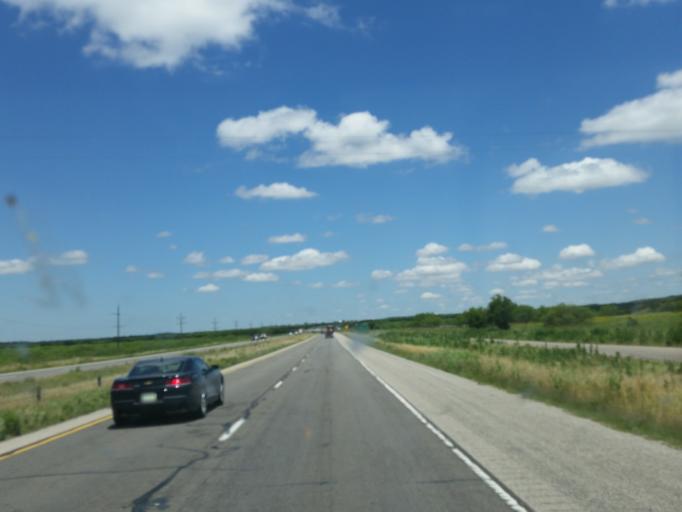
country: US
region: Texas
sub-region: Nolan County
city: Sweetwater
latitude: 32.4947
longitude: -100.2876
